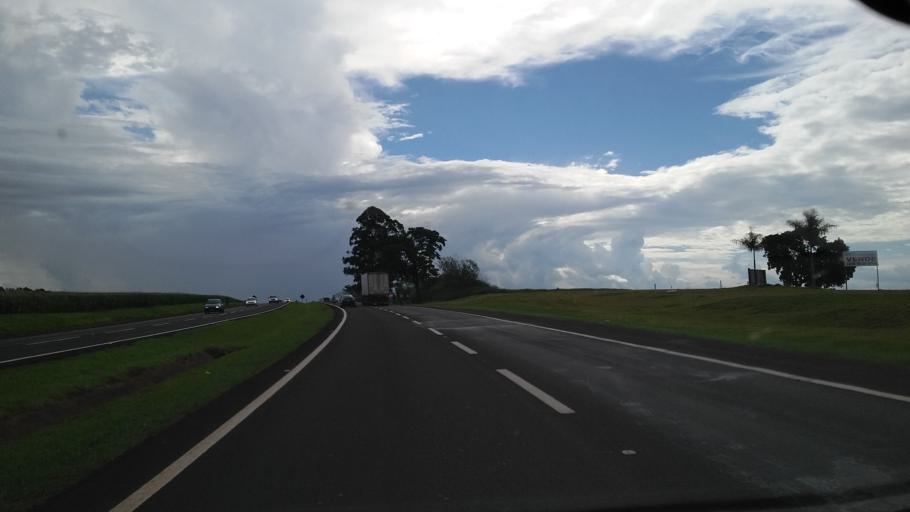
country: BR
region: Parana
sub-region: Rolandia
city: Rolandia
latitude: -23.3396
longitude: -51.3667
